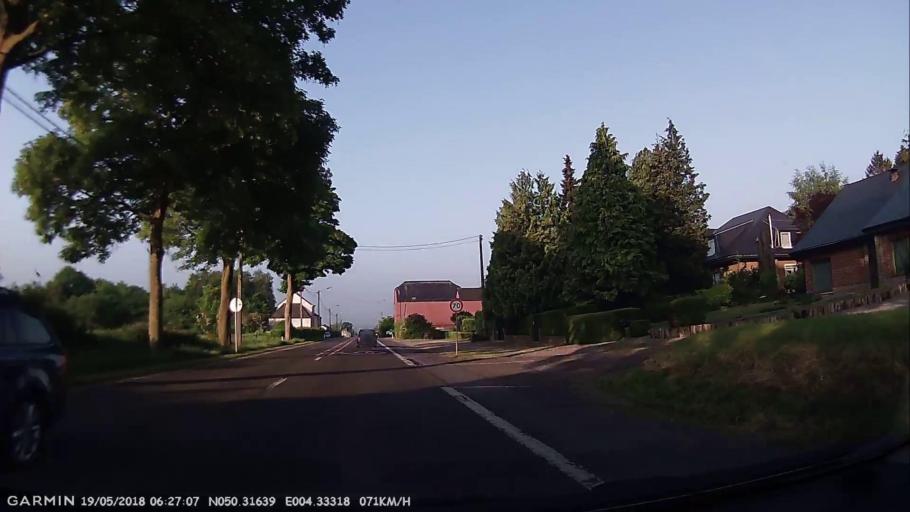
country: BE
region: Wallonia
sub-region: Province du Hainaut
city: Thuin
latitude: 50.3162
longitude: 4.3330
